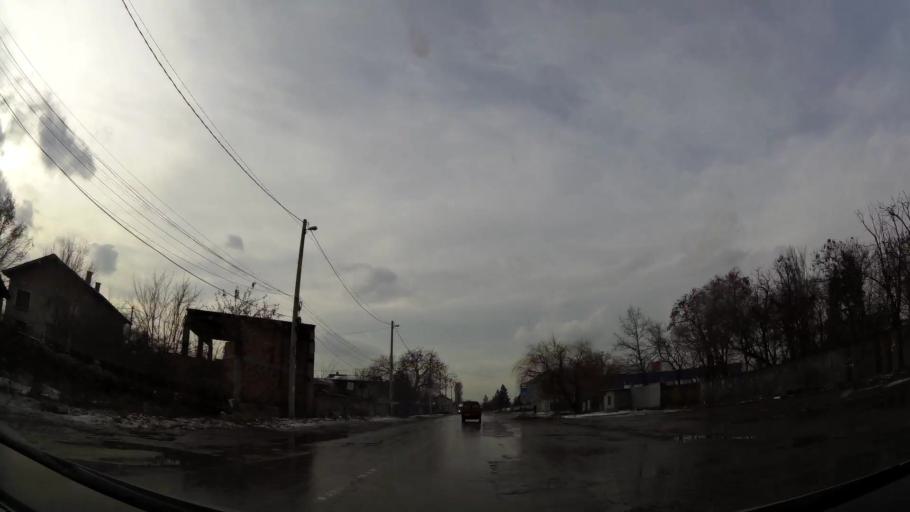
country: BG
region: Sofia-Capital
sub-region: Stolichna Obshtina
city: Sofia
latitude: 42.6931
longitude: 23.3803
